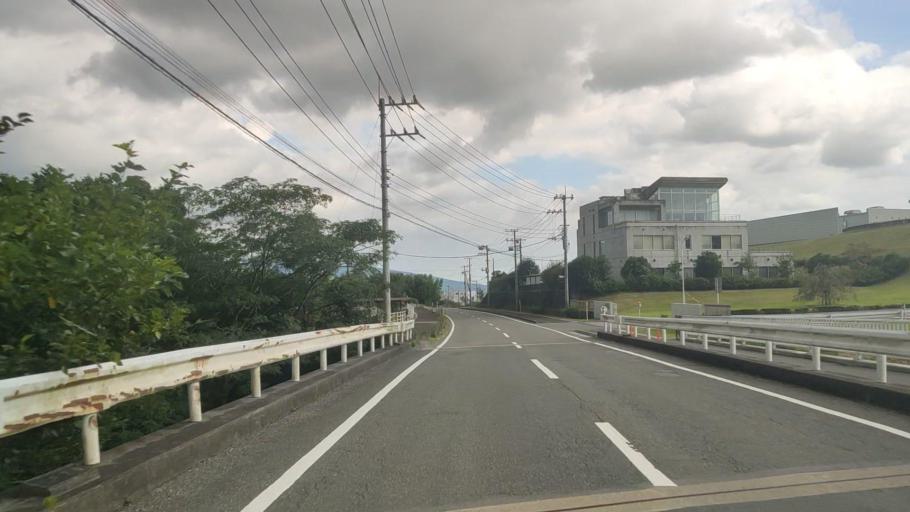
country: JP
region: Shizuoka
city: Gotemba
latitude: 35.2765
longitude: 138.8913
